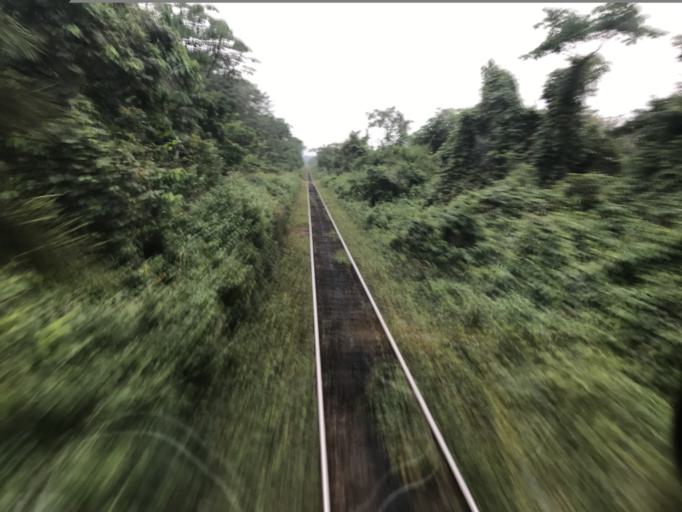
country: CM
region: Littoral
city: Edea
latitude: 3.9135
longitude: 10.1054
